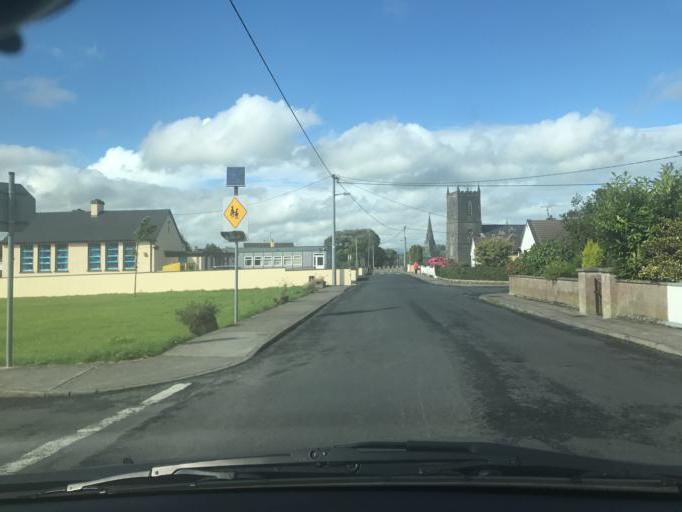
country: IE
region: Connaught
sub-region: Sligo
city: Collooney
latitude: 54.1814
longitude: -8.4920
